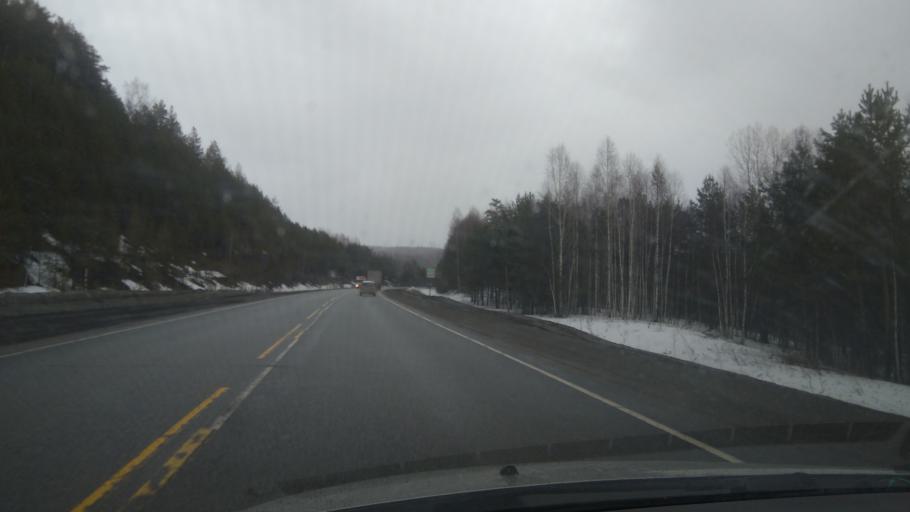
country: RU
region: Sverdlovsk
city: Ufimskiy
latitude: 56.7739
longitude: 58.2186
